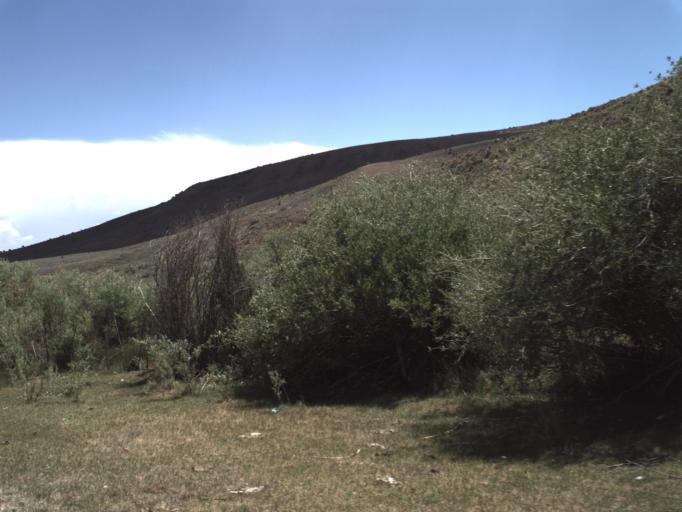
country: US
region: Utah
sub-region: Rich County
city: Randolph
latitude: 41.5036
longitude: -111.2873
